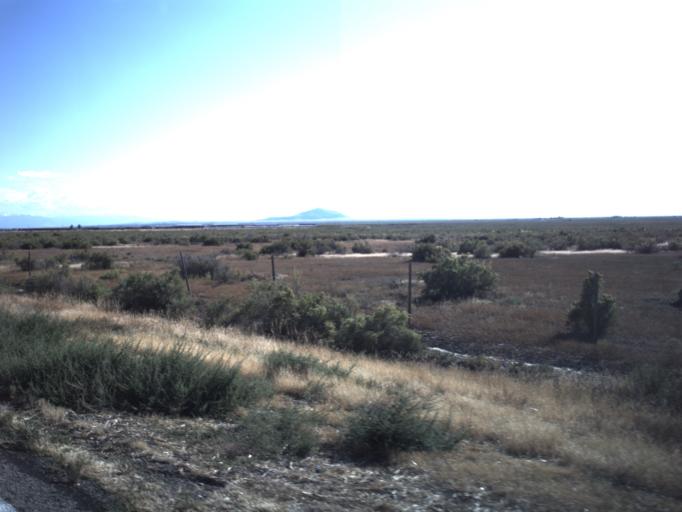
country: US
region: Utah
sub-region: Millard County
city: Delta
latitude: 39.3297
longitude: -112.4866
